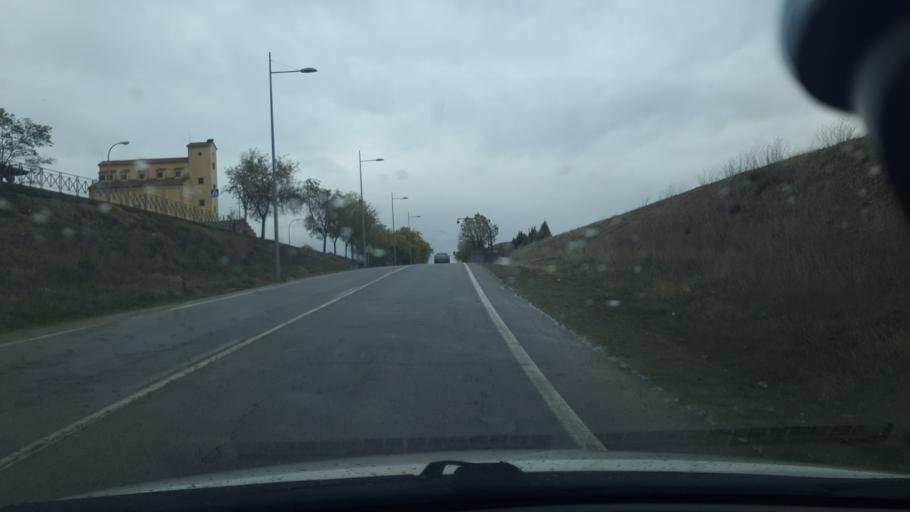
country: ES
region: Castille and Leon
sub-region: Provincia de Segovia
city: Carbonero el Mayor
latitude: 41.1144
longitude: -4.2601
